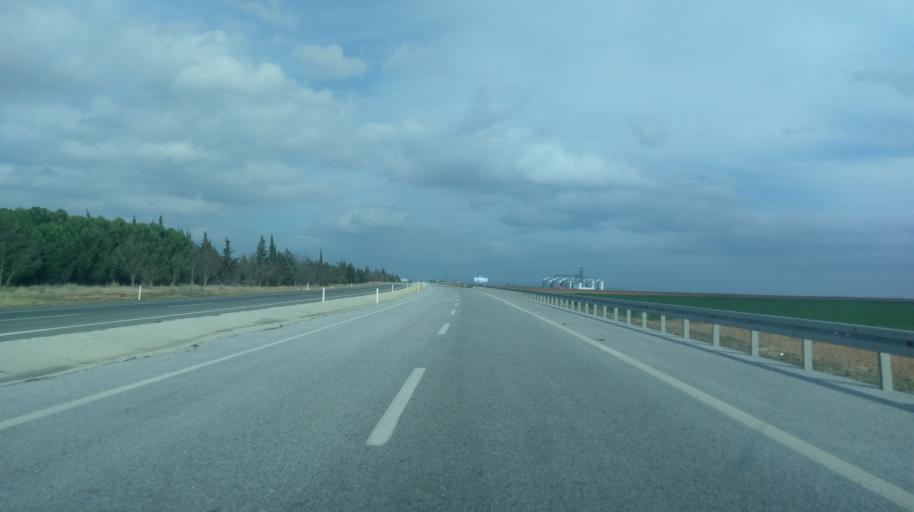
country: TR
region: Kirklareli
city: Kirklareli
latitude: 41.6990
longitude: 27.1542
